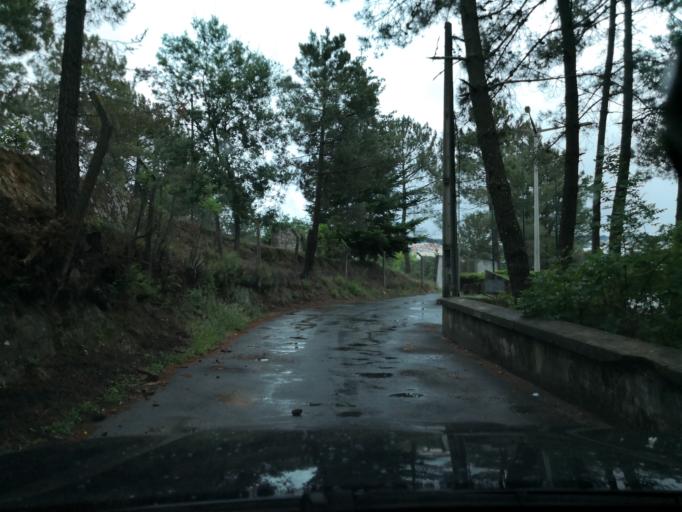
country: PT
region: Vila Real
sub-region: Vila Real
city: Vila Real
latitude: 41.3023
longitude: -7.7365
